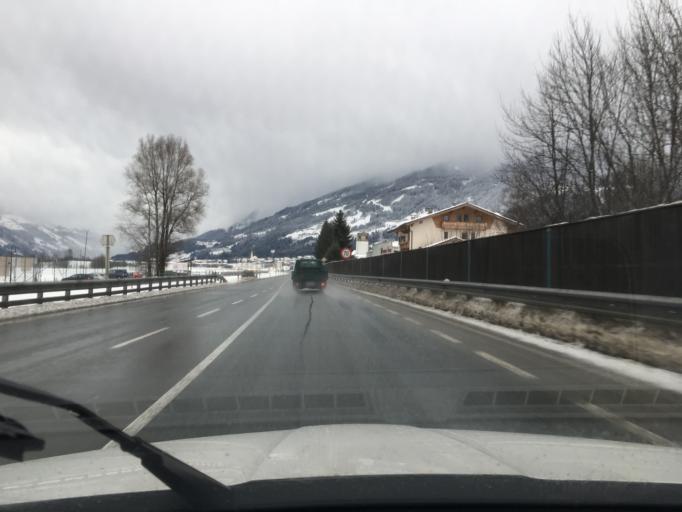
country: AT
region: Tyrol
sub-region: Politischer Bezirk Schwaz
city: Uderns
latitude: 47.3208
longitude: 11.8651
